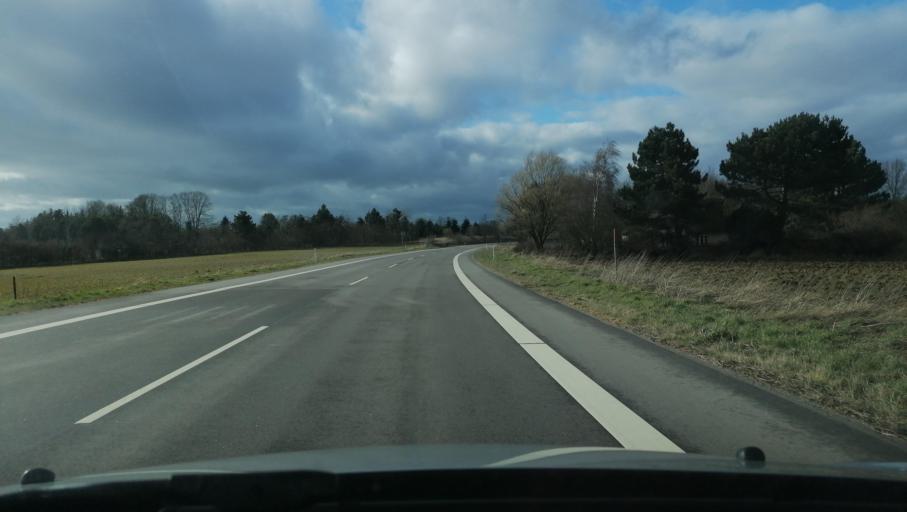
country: DK
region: Zealand
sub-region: Odsherred Kommune
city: Horve
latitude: 55.7659
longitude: 11.4296
